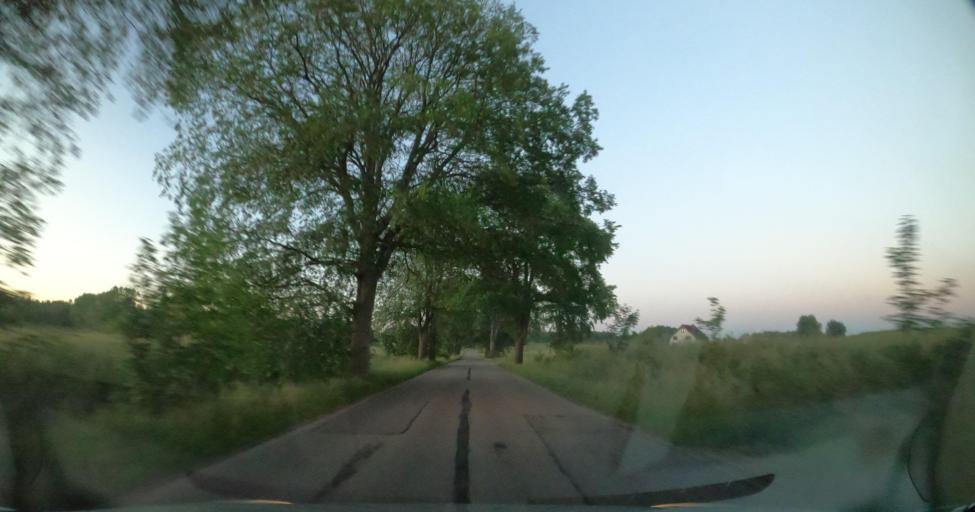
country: PL
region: Pomeranian Voivodeship
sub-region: Powiat wejherowski
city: Szemud
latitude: 54.4684
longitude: 18.1480
